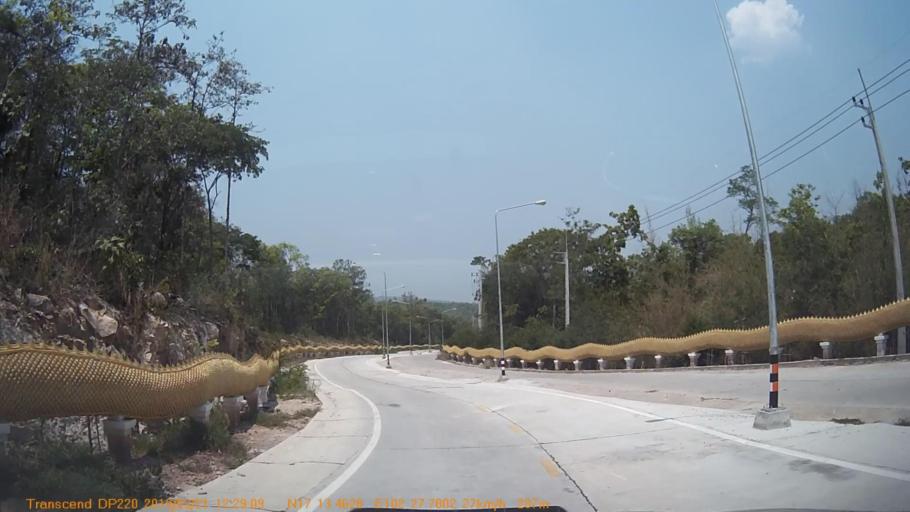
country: TH
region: Changwat Nong Bua Lamphu
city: Nong Bua Lamphu
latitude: 17.2244
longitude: 102.4630
